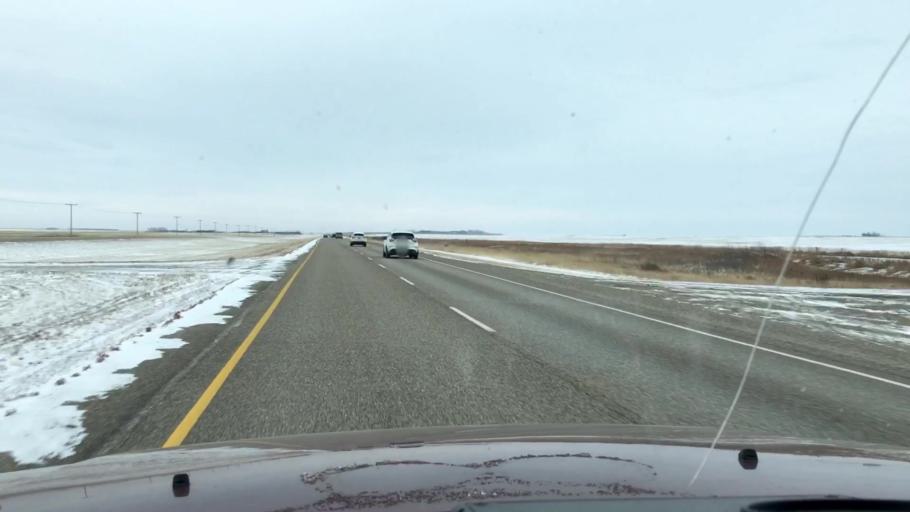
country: CA
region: Saskatchewan
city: Moose Jaw
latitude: 50.9975
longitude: -105.7607
